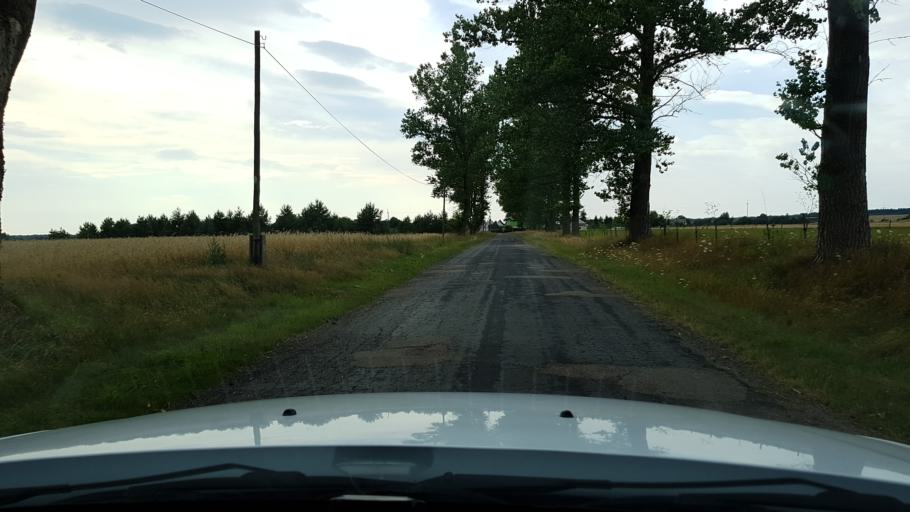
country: PL
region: West Pomeranian Voivodeship
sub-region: Powiat drawski
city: Czaplinek
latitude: 53.4376
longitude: 16.2809
